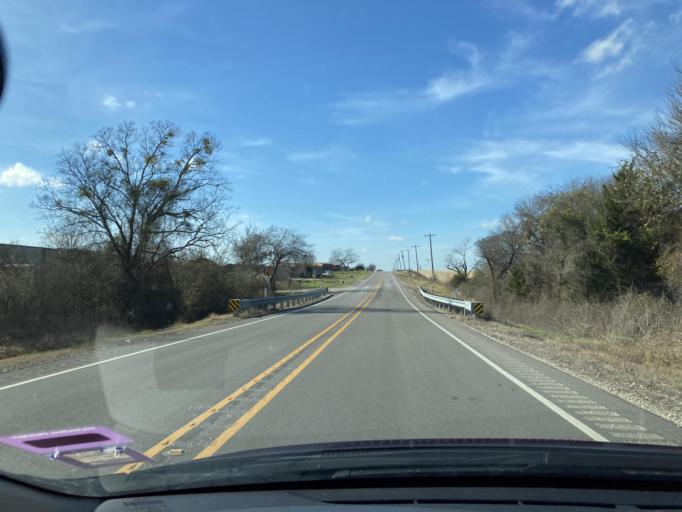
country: US
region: Texas
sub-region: Navarro County
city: Corsicana
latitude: 32.0544
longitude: -96.3683
